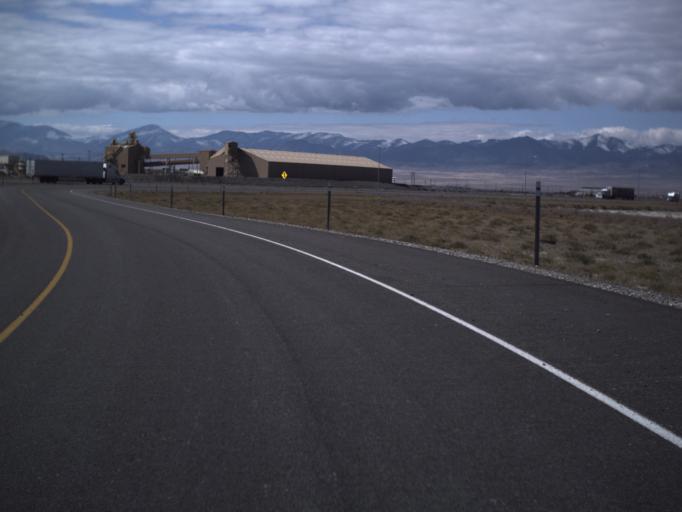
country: US
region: Utah
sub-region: Tooele County
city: Wendover
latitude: 40.7441
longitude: -113.9715
